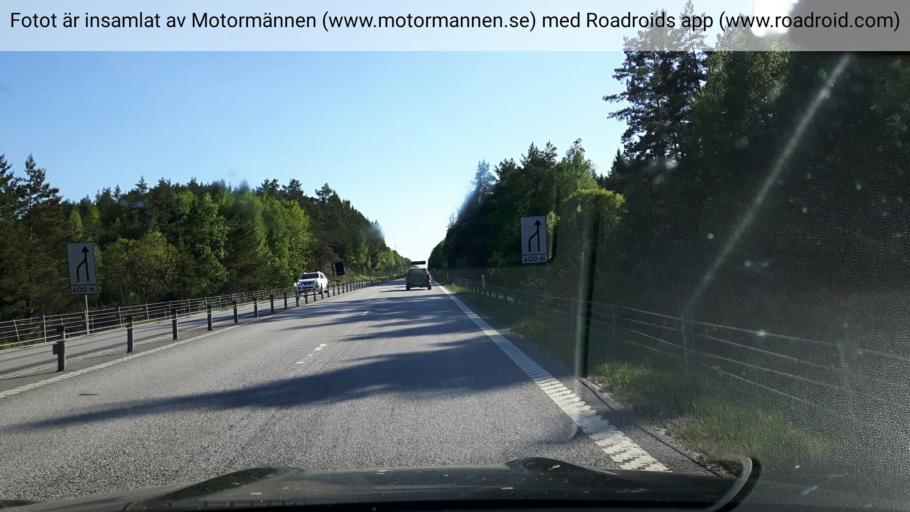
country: SE
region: Stockholm
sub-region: Osterakers Kommun
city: Akersberga
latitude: 59.5448
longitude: 18.2198
